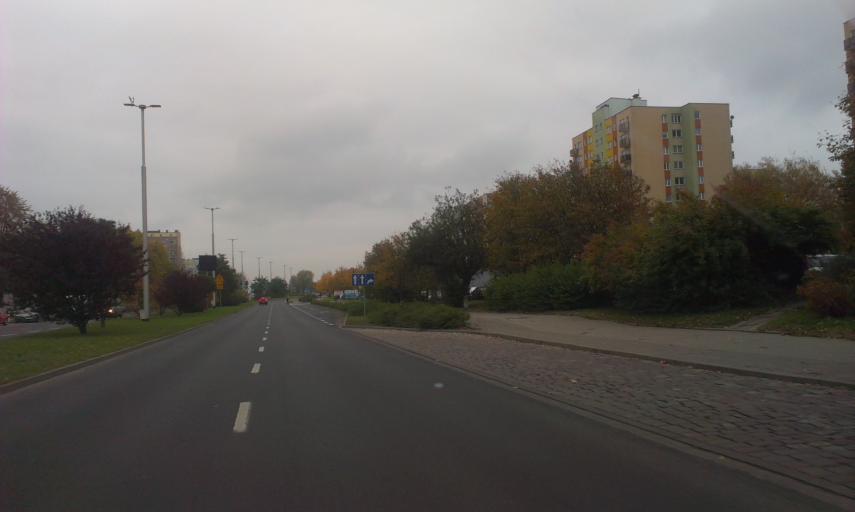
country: PL
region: West Pomeranian Voivodeship
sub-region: Koszalin
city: Koszalin
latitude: 54.2024
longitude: 16.1852
